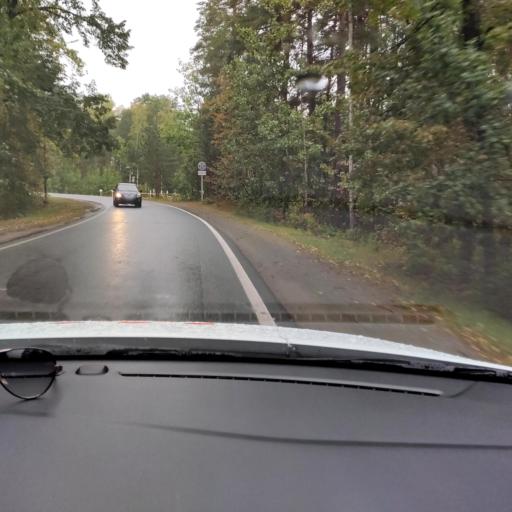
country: RU
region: Tatarstan
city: Verkhniy Uslon
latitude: 55.6403
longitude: 49.0216
